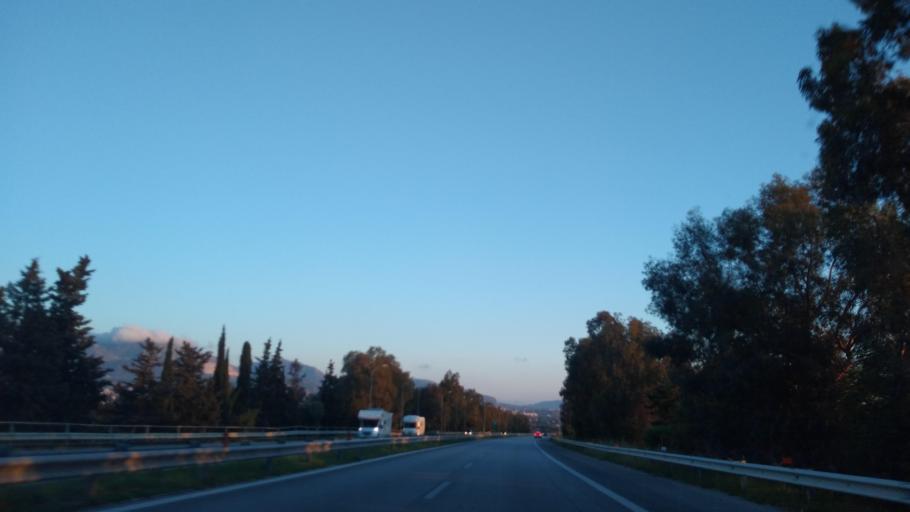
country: IT
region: Sicily
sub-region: Palermo
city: Agliandroni-Paternella
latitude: 38.0923
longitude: 13.0963
